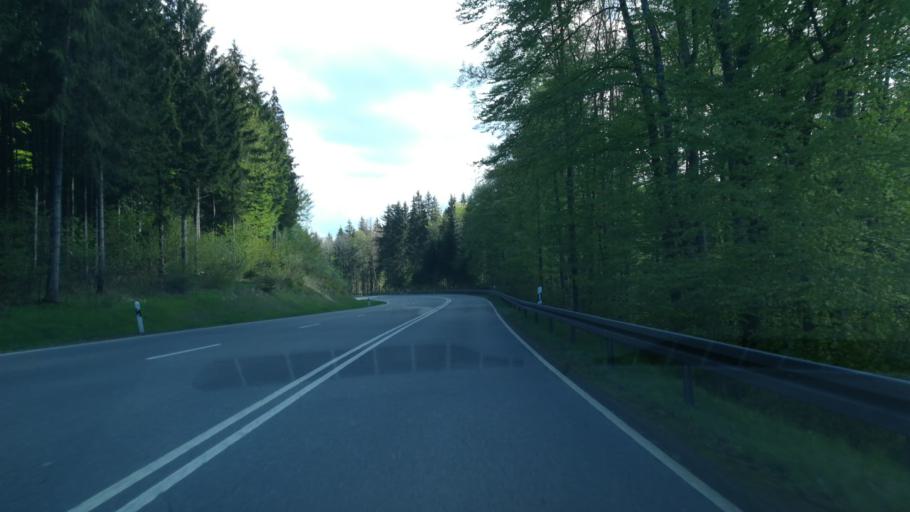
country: DE
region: Baden-Wuerttemberg
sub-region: Freiburg Region
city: Blumberg
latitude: 47.8279
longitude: 8.5634
